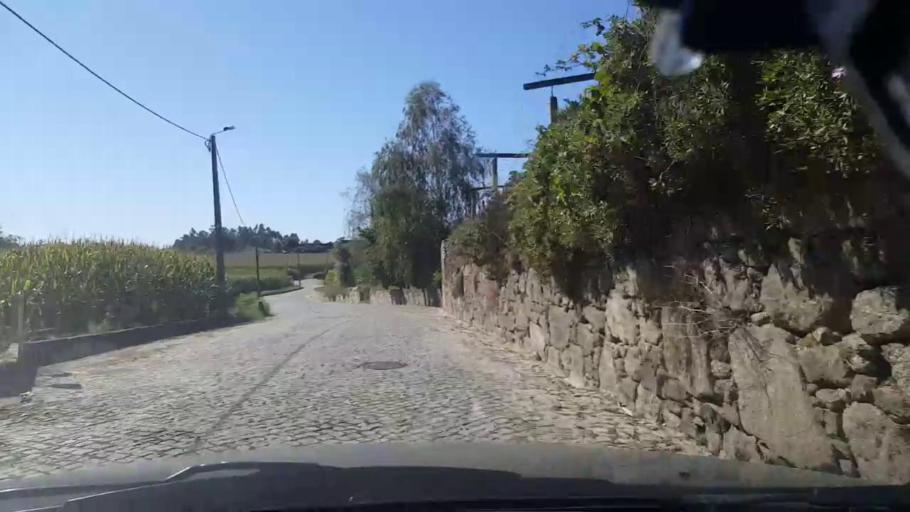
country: PT
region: Porto
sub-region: Maia
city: Gemunde
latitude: 41.2983
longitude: -8.6703
